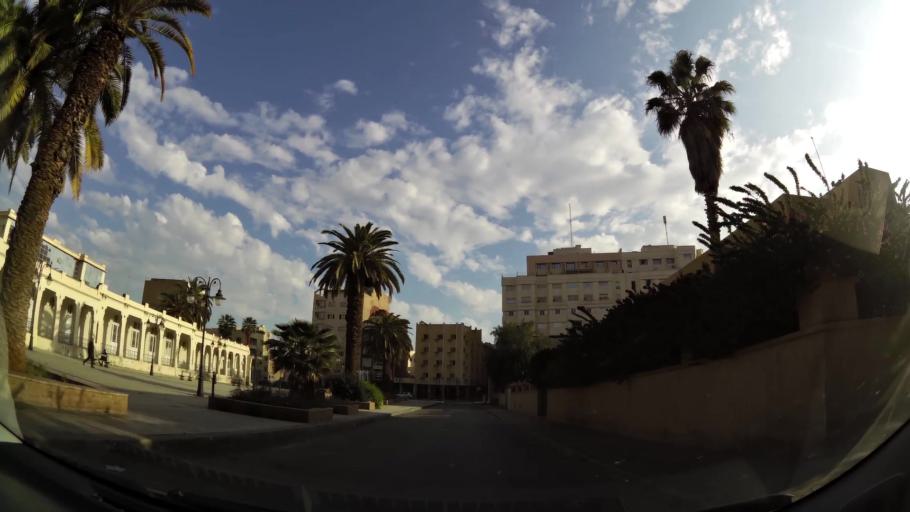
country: MA
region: Oriental
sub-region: Oujda-Angad
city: Oujda
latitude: 34.6800
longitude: -1.9205
